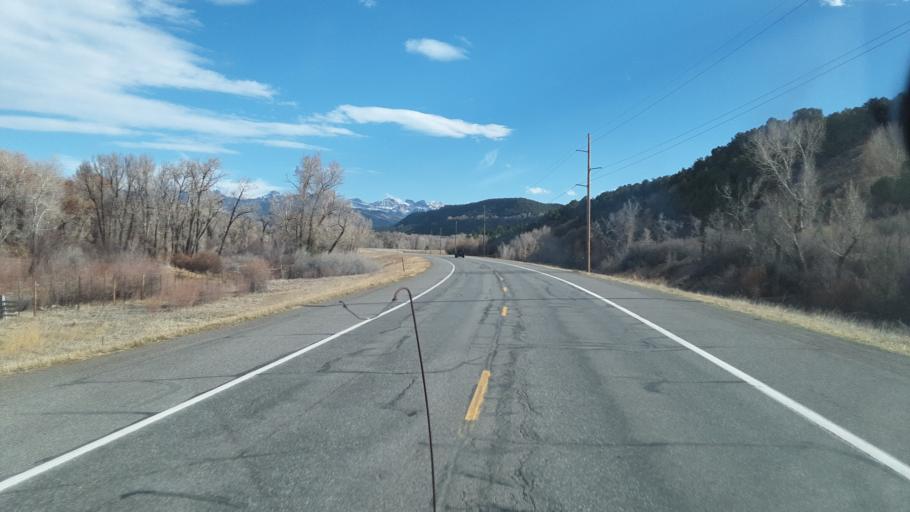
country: US
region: Colorado
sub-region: Ouray County
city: Ouray
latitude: 38.2355
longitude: -107.7364
